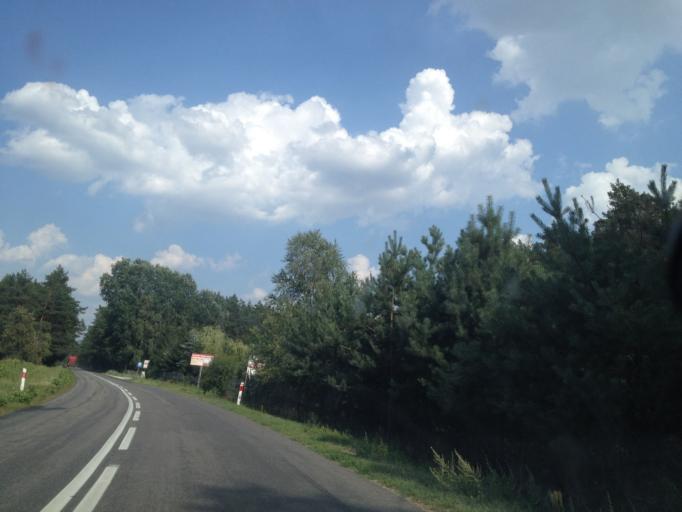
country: PL
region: Greater Poland Voivodeship
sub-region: Powiat poznanski
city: Daszewice
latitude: 52.2303
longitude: 16.9793
